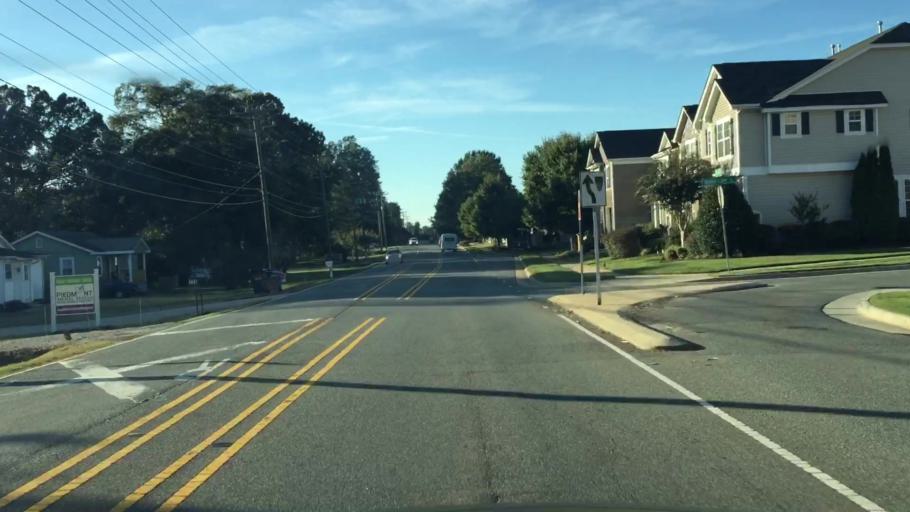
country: US
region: North Carolina
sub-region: Iredell County
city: Mooresville
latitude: 35.5559
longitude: -80.8434
